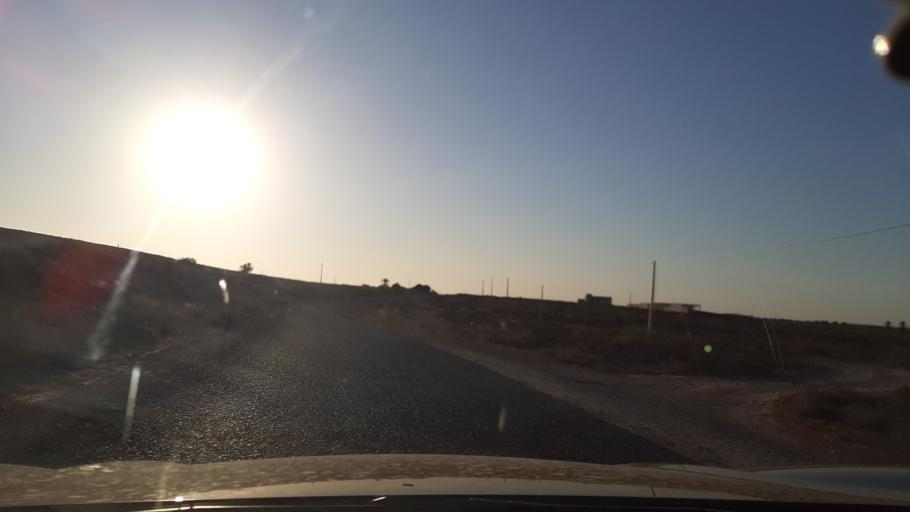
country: TN
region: Qabis
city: Matmata
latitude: 33.6216
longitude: 10.1418
